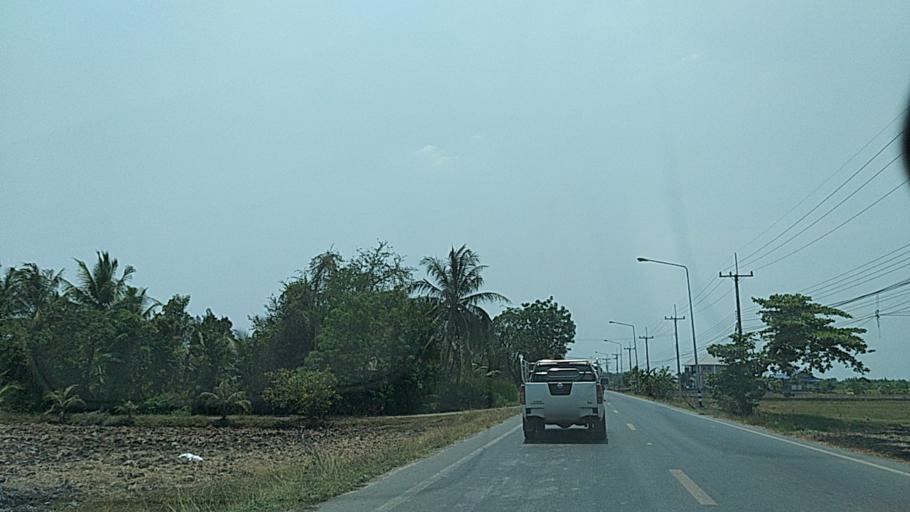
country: TH
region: Chachoengsao
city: Bang Nam Priao
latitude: 13.8585
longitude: 100.9659
